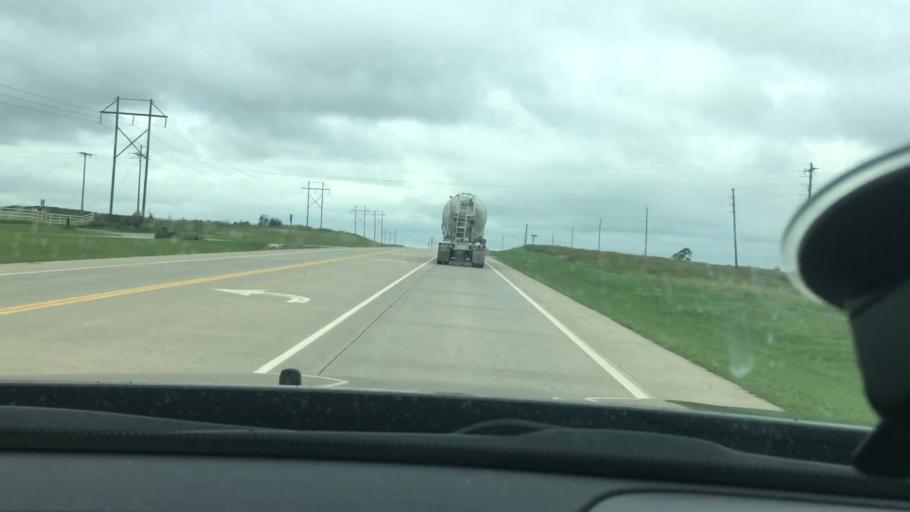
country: US
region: Oklahoma
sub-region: Pontotoc County
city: Ada
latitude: 34.6518
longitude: -96.8260
